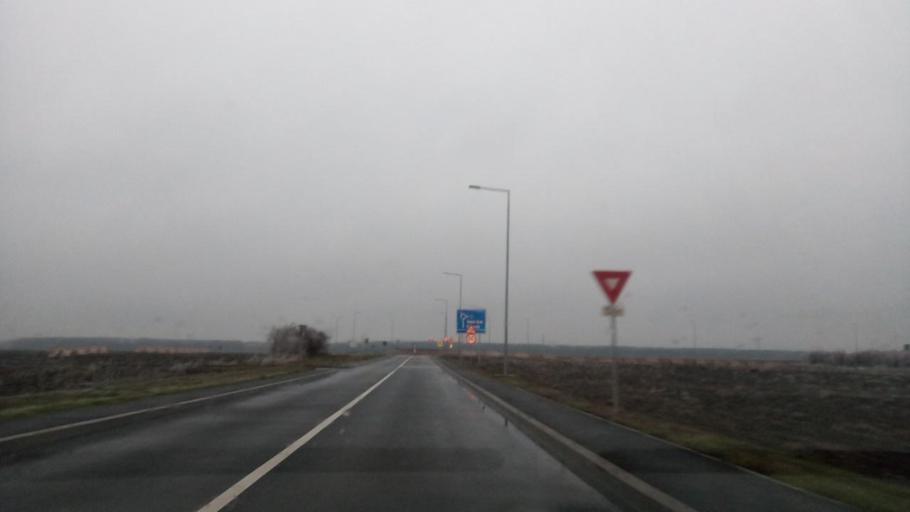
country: RO
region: Ilfov
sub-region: Comuna Branesti
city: Branesti
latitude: 44.4303
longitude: 26.3603
